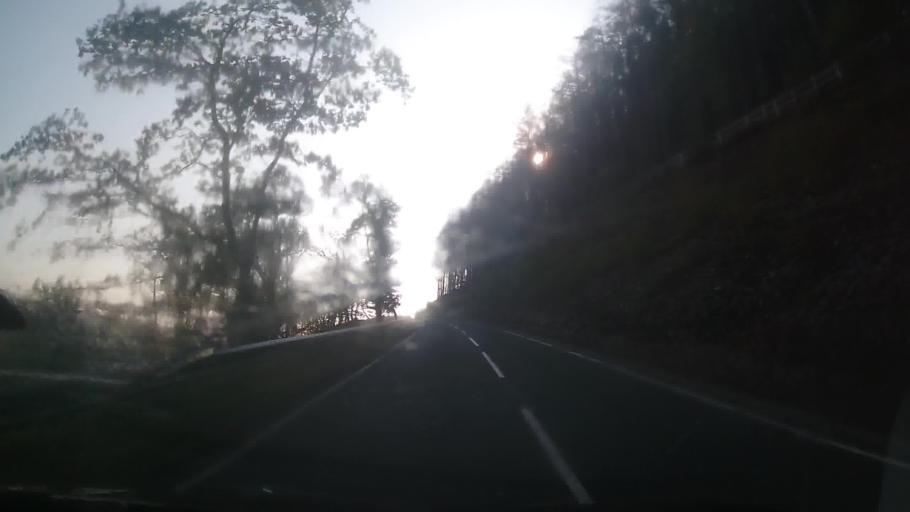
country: GB
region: Wales
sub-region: County of Ceredigion
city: Lledrod
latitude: 52.3441
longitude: -3.8368
